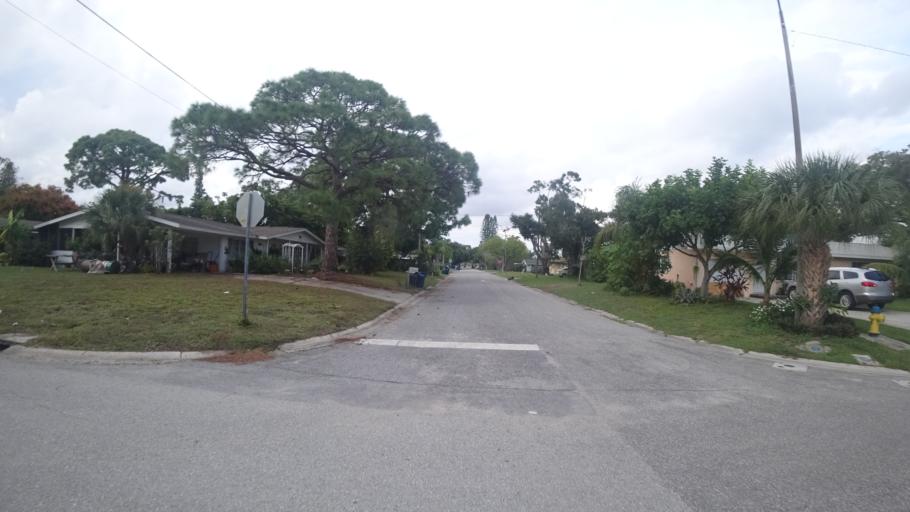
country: US
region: Florida
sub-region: Manatee County
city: South Bradenton
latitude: 27.4562
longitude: -82.5810
